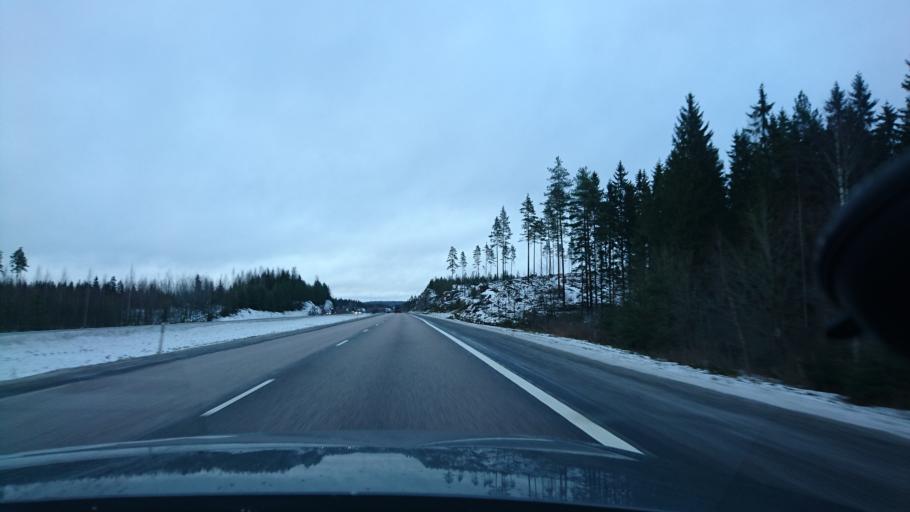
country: FI
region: Uusimaa
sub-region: Porvoo
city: Pukkila
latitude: 60.7500
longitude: 25.4583
